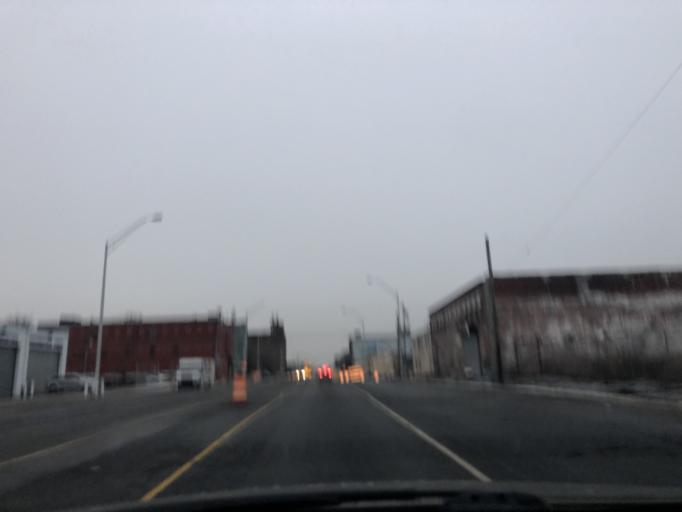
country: US
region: Pennsylvania
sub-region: Philadelphia County
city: Philadelphia
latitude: 39.9845
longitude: -75.1376
